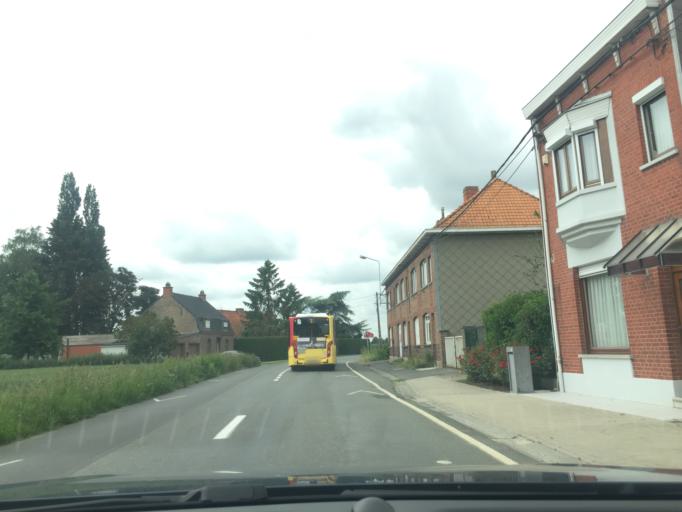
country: BE
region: Wallonia
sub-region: Province du Hainaut
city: Estaimpuis
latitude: 50.6903
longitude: 3.2835
